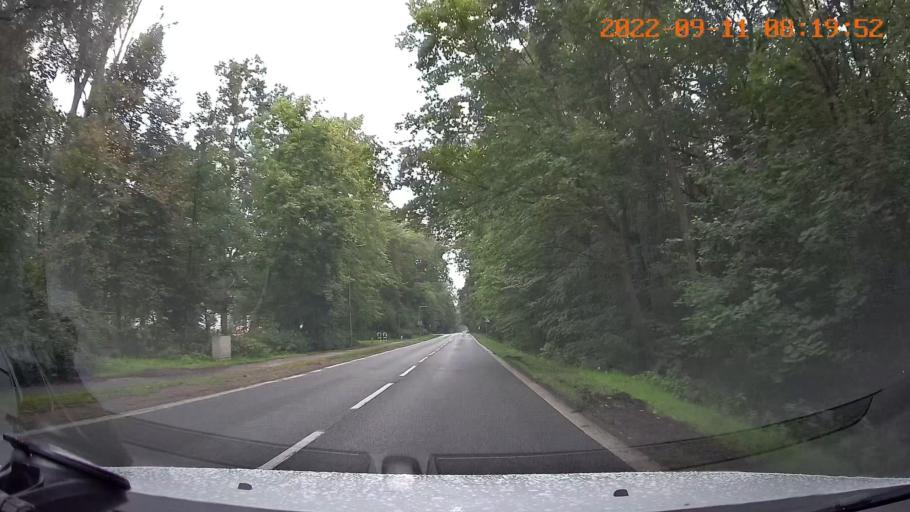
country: PL
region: Silesian Voivodeship
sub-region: Tychy
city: Tychy
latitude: 50.1547
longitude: 19.0076
